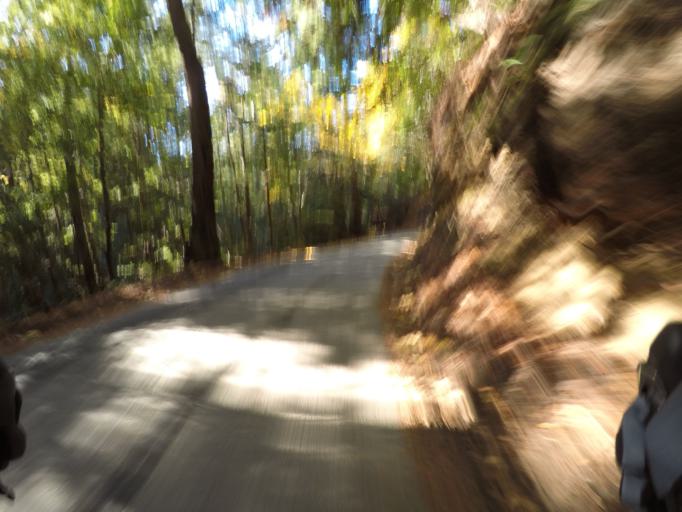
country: US
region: California
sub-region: Santa Clara County
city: Lexington Hills
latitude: 37.1541
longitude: -122.0121
